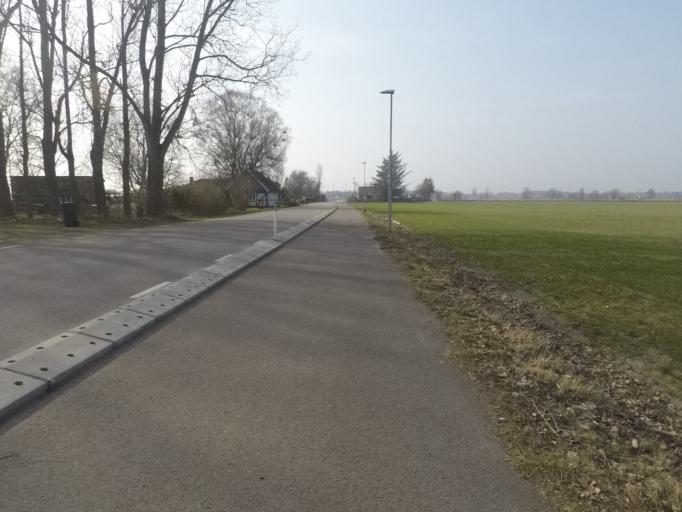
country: SE
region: Skane
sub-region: Helsingborg
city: Odakra
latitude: 56.2156
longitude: 12.6893
